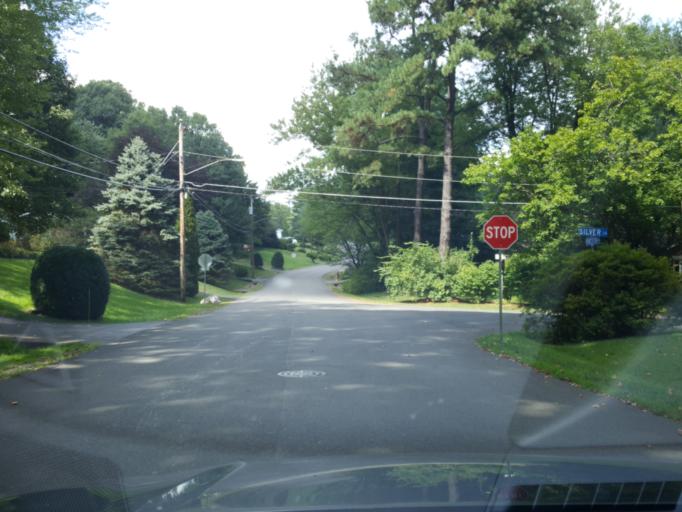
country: US
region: Virginia
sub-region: Fairfax County
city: Annandale
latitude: 38.8174
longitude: -77.1827
